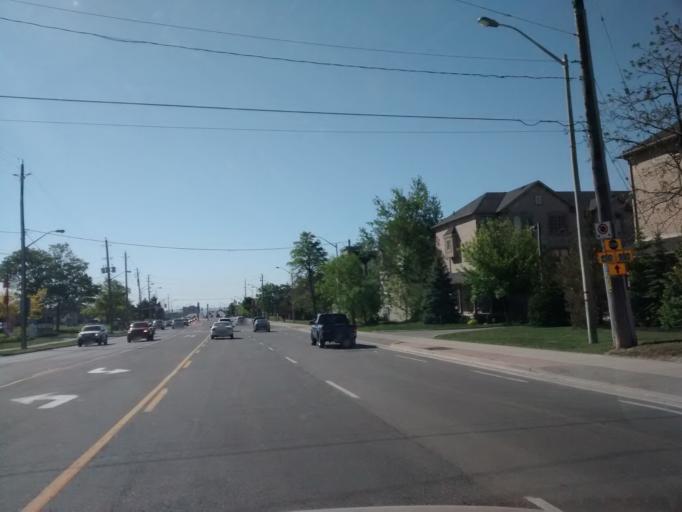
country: CA
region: Ontario
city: Burlington
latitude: 43.3583
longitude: -79.8128
